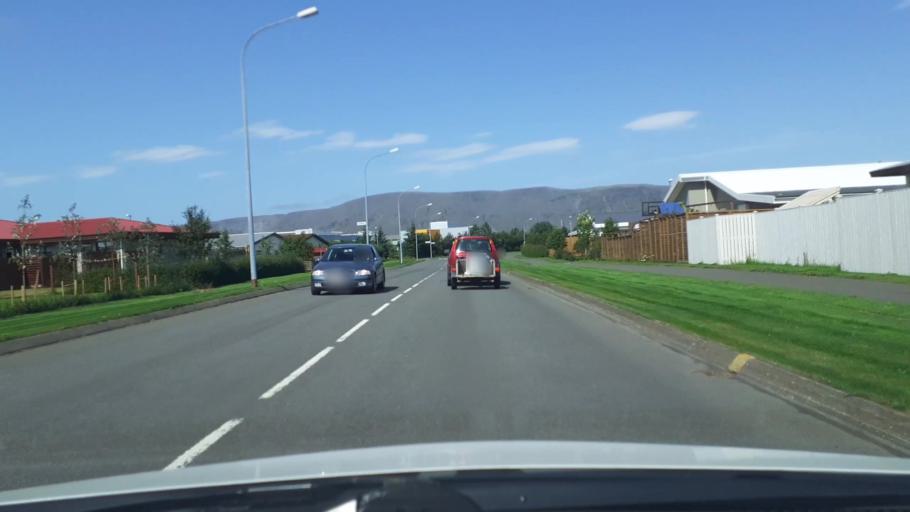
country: IS
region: South
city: Selfoss
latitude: 63.9235
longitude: -20.9922
